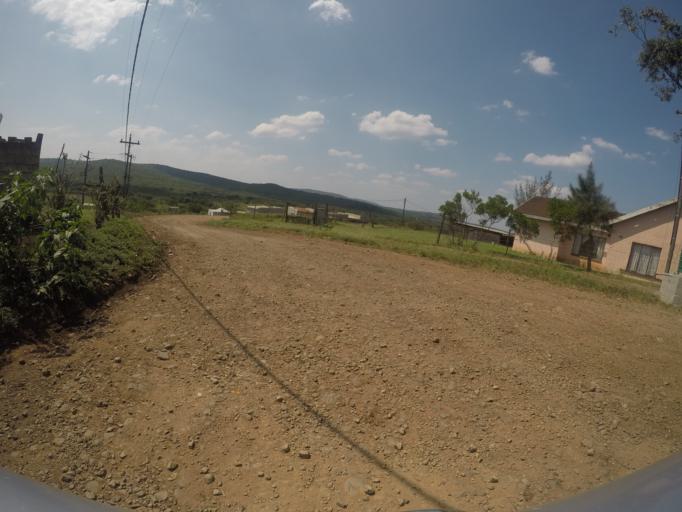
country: ZA
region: KwaZulu-Natal
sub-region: uThungulu District Municipality
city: Empangeni
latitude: -28.5888
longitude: 31.7429
